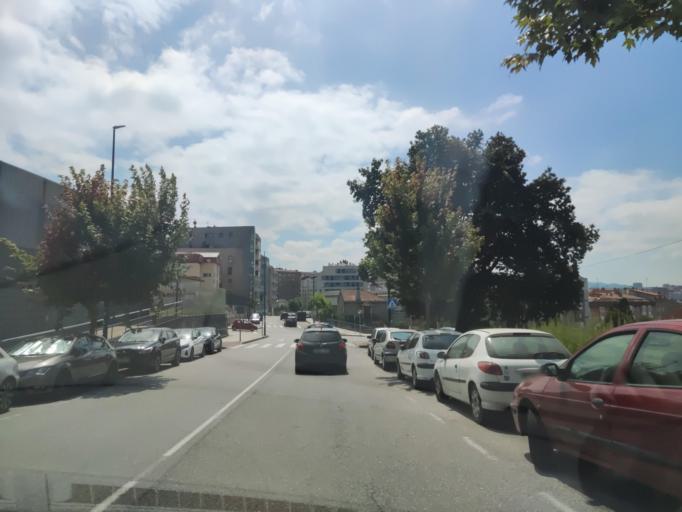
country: ES
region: Galicia
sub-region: Provincia de Pontevedra
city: Vigo
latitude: 42.2515
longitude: -8.6986
